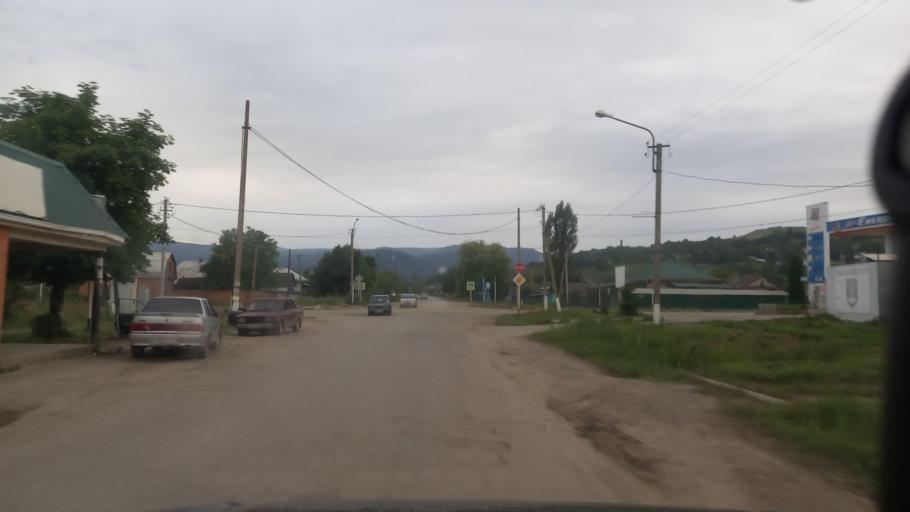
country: RU
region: Karachayevo-Cherkesiya
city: Pregradnaya
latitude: 43.9413
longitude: 41.1818
